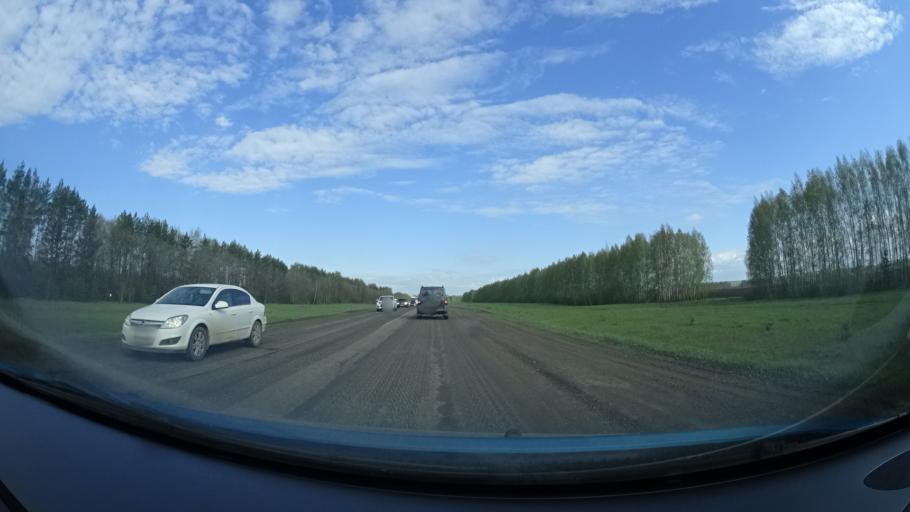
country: RU
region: Bashkortostan
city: Blagoveshchensk
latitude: 55.2359
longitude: 55.7763
